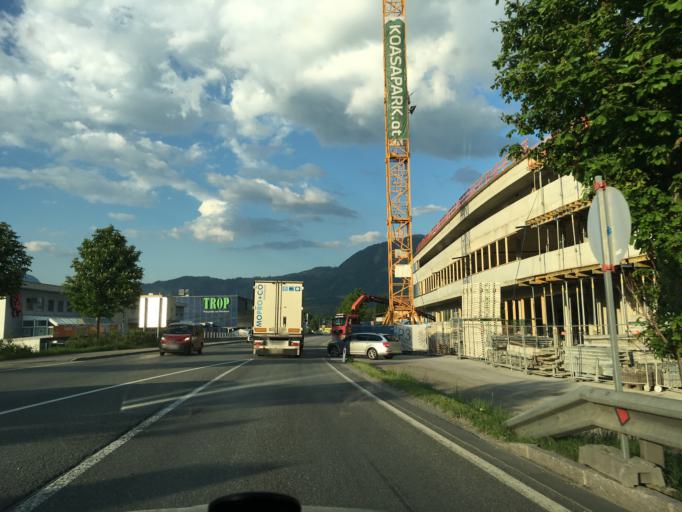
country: AT
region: Tyrol
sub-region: Politischer Bezirk Kitzbuhel
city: Sankt Johann in Tirol
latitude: 47.5185
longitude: 12.4140
